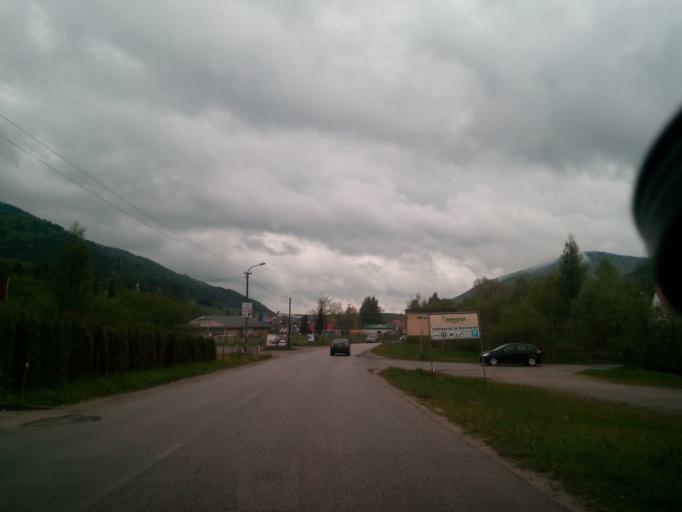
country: SK
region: Zilinsky
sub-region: Okres Zilina
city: Terchova
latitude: 49.2568
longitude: 19.0435
